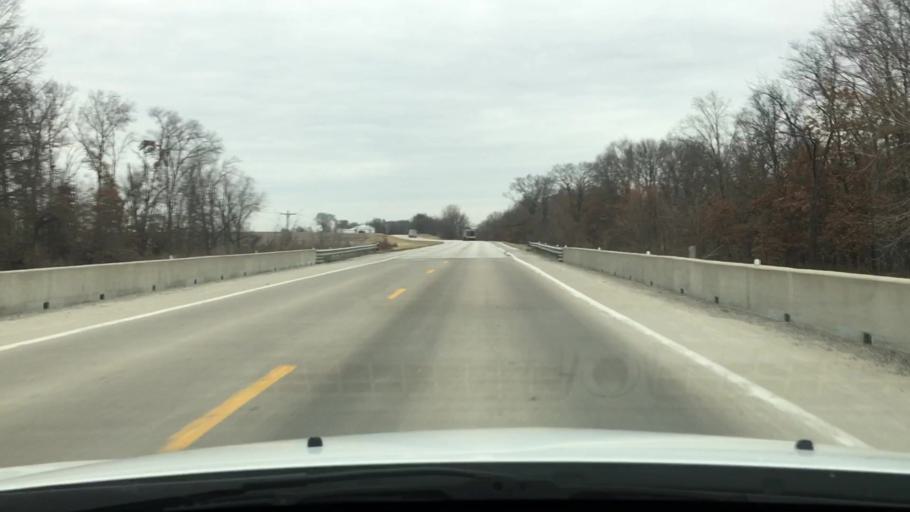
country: US
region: Missouri
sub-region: Montgomery County
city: Wellsville
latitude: 39.2001
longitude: -91.6464
